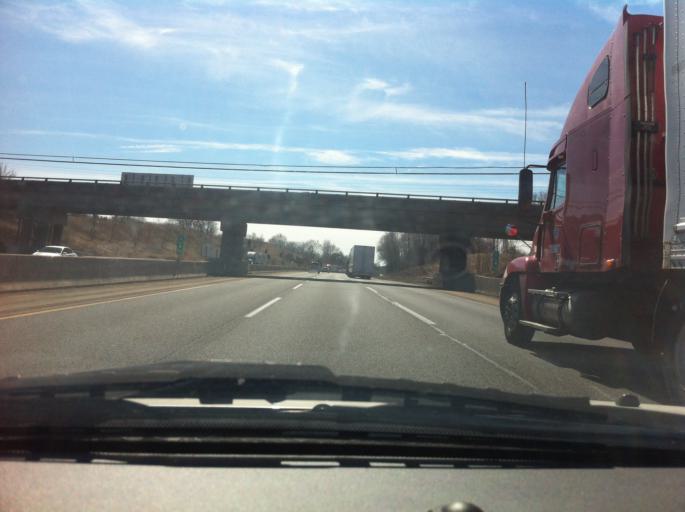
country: US
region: Wisconsin
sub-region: Rock County
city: Beloit
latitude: 42.4991
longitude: -88.9920
